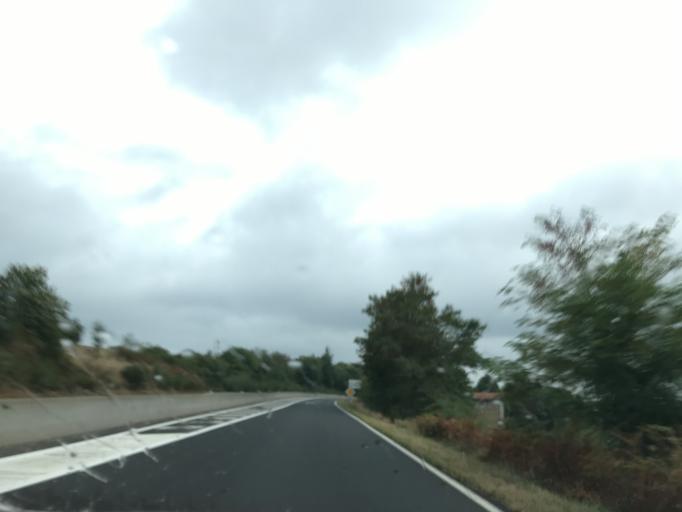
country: FR
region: Auvergne
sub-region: Departement du Puy-de-Dome
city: Courpiere
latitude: 45.7208
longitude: 3.5823
